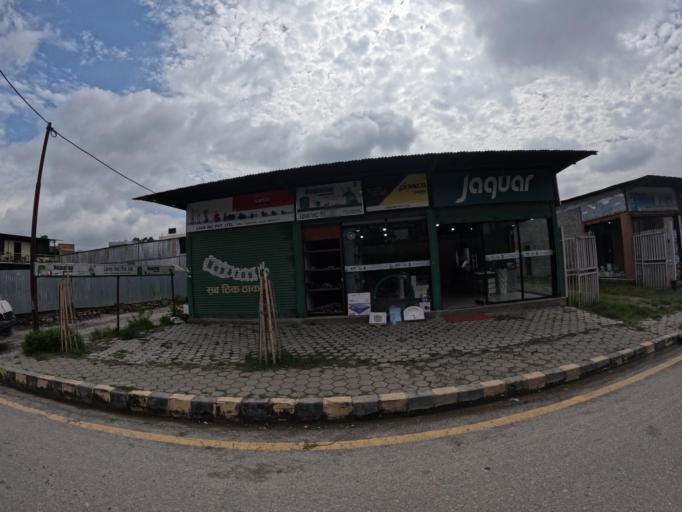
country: NP
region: Central Region
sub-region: Bagmati Zone
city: Kathmandu
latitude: 27.7584
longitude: 85.3161
